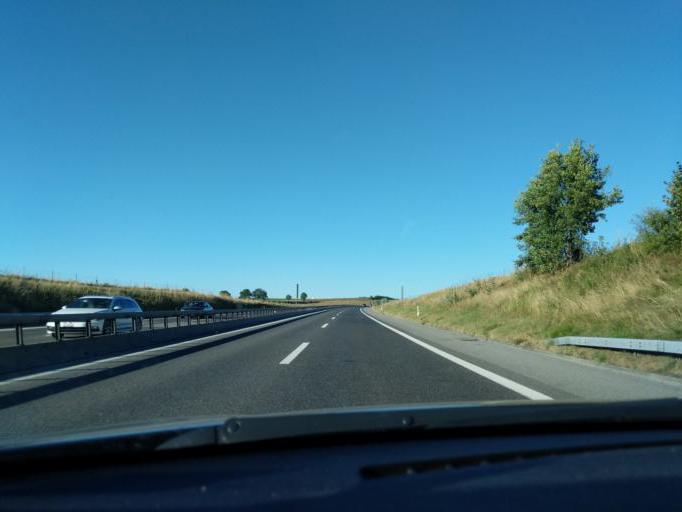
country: CH
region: Fribourg
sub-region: Sense District
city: Ueberstorf
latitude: 46.8811
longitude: 7.2849
